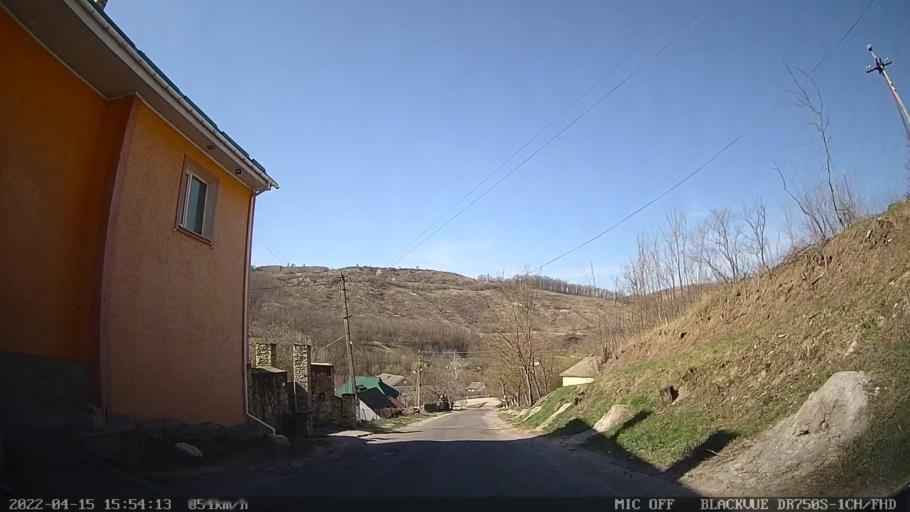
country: MD
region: Raionul Ocnita
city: Otaci
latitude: 48.4025
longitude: 27.8908
